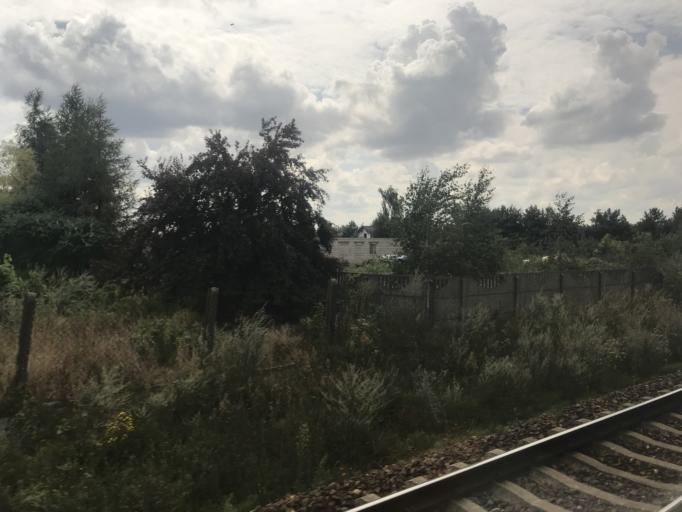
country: PL
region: Greater Poland Voivodeship
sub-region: Powiat poznanski
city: Dopiewo
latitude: 52.3652
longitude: 16.7102
